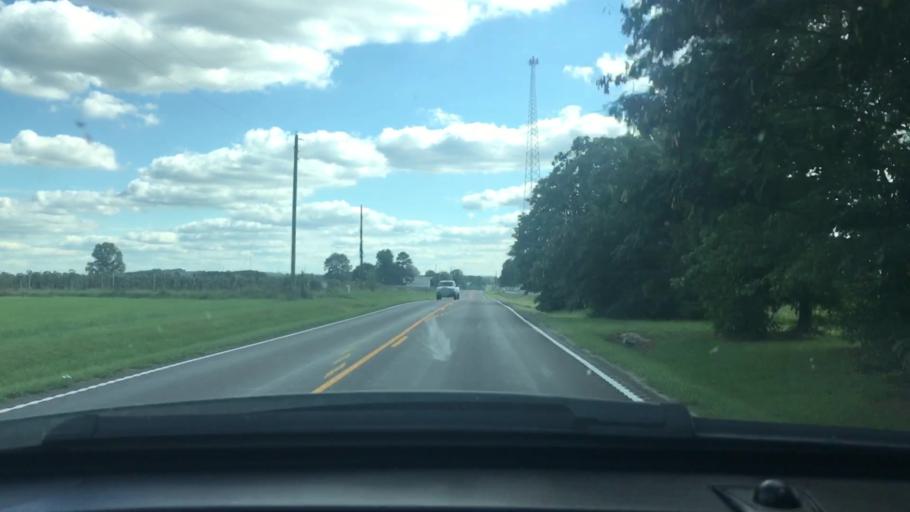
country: US
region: Missouri
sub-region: Wright County
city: Mountain Grove
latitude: 37.2503
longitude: -92.3003
